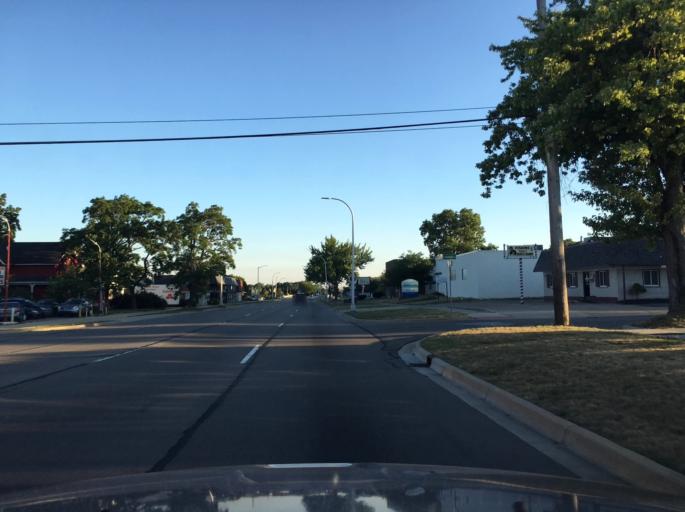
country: US
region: Michigan
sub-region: Macomb County
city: Mount Clemens
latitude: 42.5879
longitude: -82.8823
